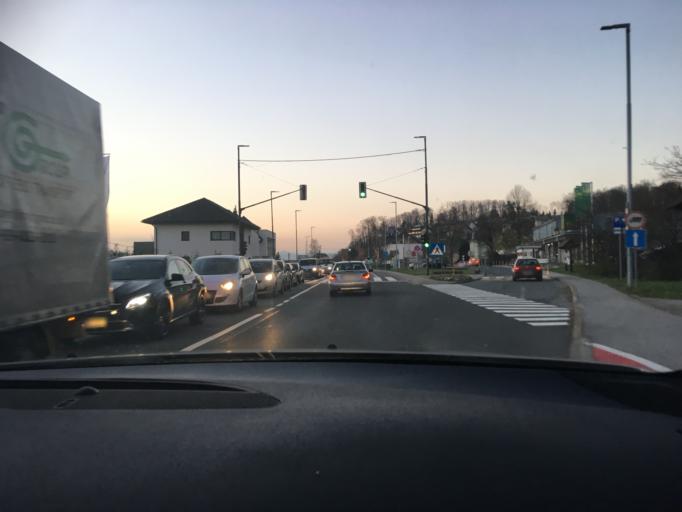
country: SI
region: Skofljica
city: Skofljica
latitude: 45.9849
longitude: 14.5735
